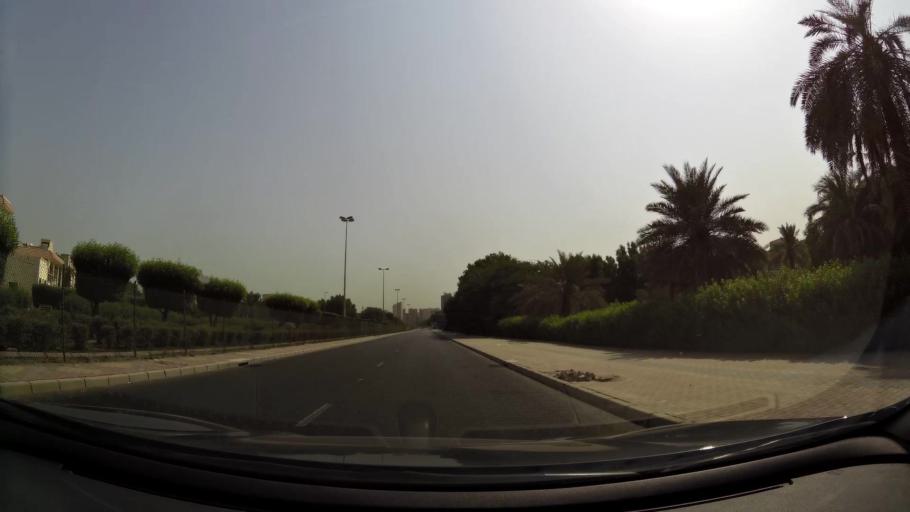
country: KW
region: Al Asimah
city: Ad Dasmah
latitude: 29.3535
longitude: 48.0078
